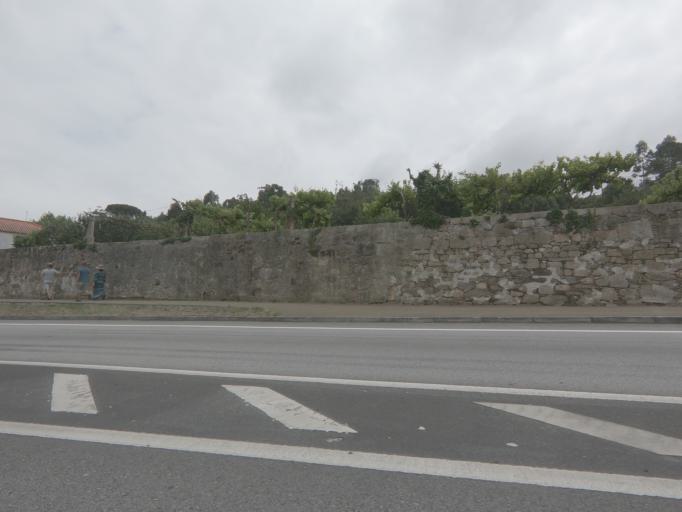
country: PT
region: Viana do Castelo
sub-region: Vila Nova de Cerveira
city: Vila Nova de Cerveira
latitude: 41.9455
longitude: -8.7405
